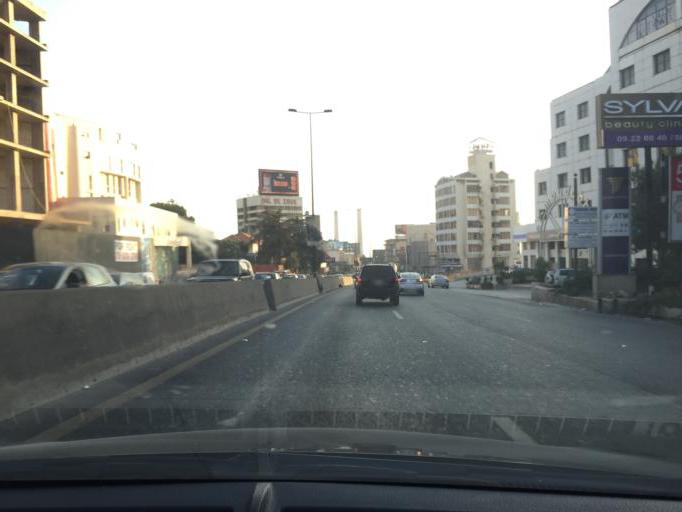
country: LB
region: Mont-Liban
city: Djounie
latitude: 33.9767
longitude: 35.6162
